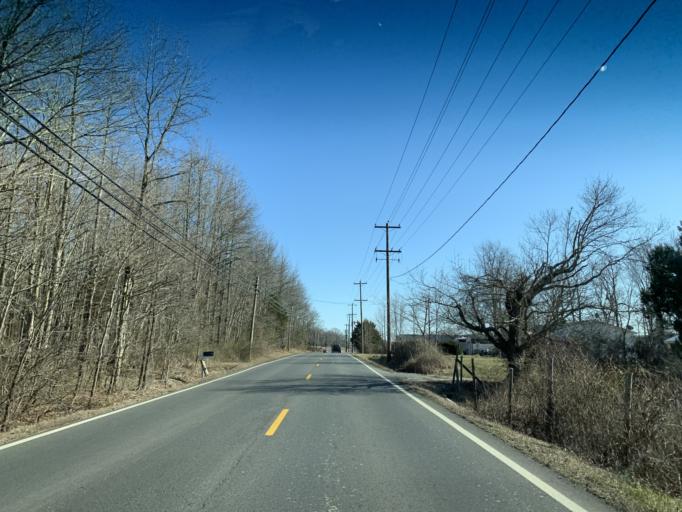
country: US
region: Maryland
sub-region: Cecil County
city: Elkton
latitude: 39.6251
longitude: -75.8544
